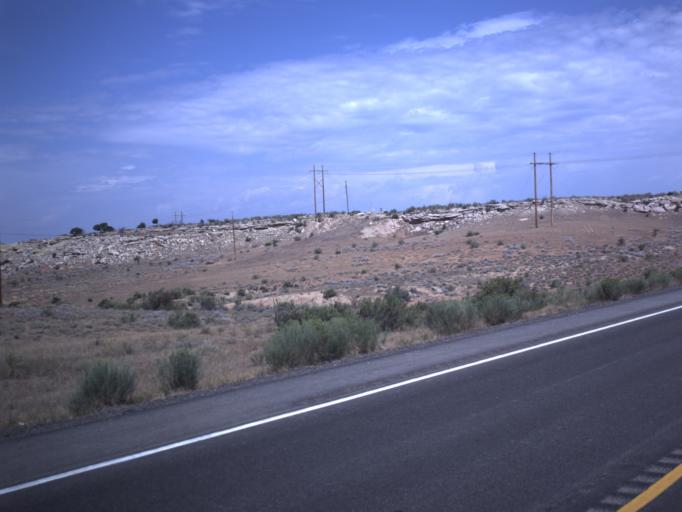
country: US
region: Utah
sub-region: Uintah County
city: Naples
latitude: 40.1896
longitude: -109.3309
